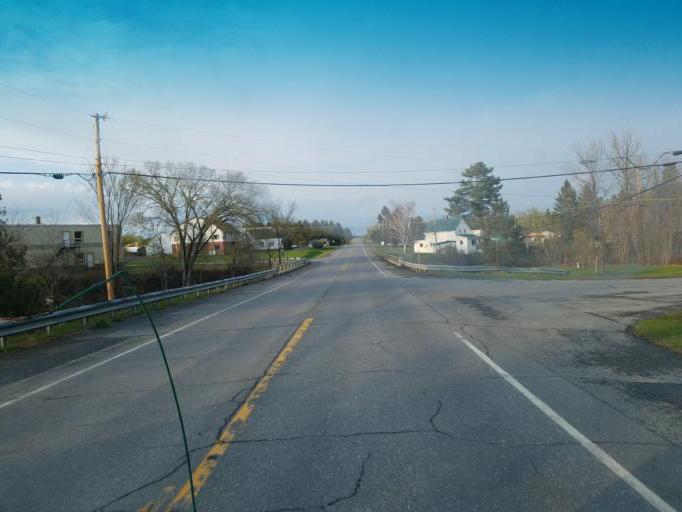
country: US
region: Maine
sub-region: Aroostook County
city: Caribou
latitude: 46.8481
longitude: -68.0437
